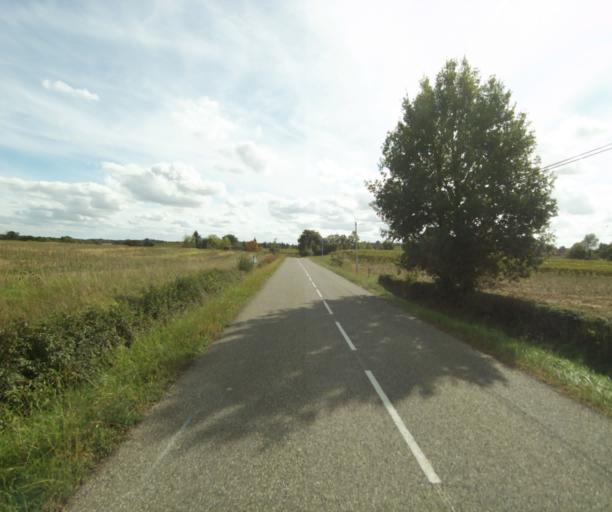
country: FR
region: Midi-Pyrenees
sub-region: Departement du Gers
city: Eauze
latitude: 43.8403
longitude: 0.1505
